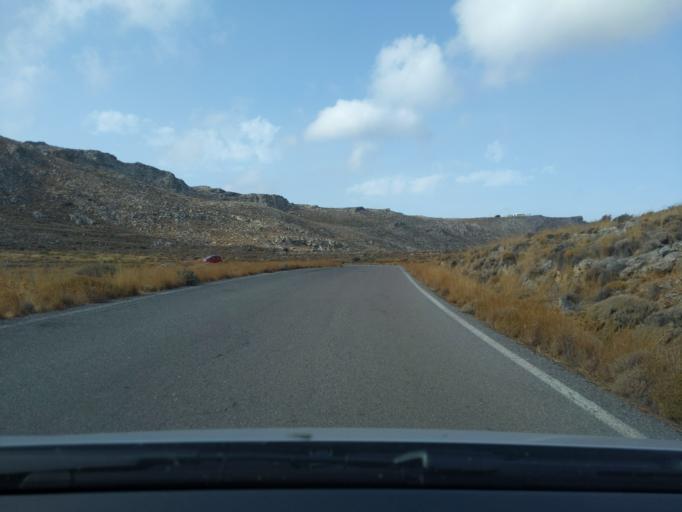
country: GR
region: Crete
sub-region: Nomos Lasithiou
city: Palekastro
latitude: 35.0914
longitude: 26.2629
